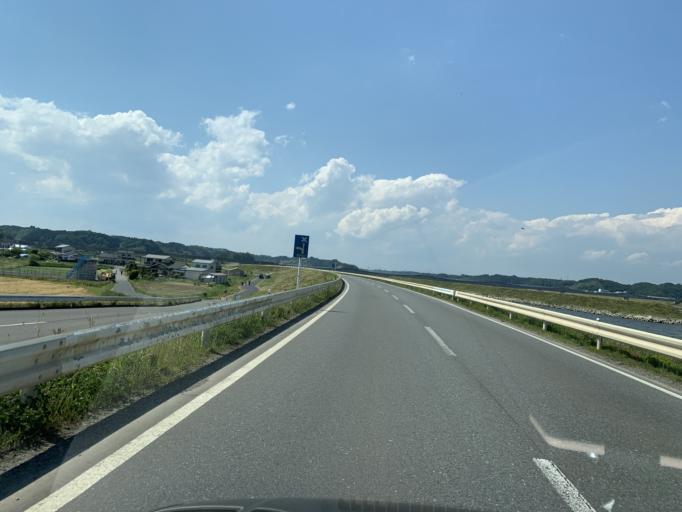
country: JP
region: Miyagi
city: Yamoto
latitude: 38.3843
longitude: 141.1673
